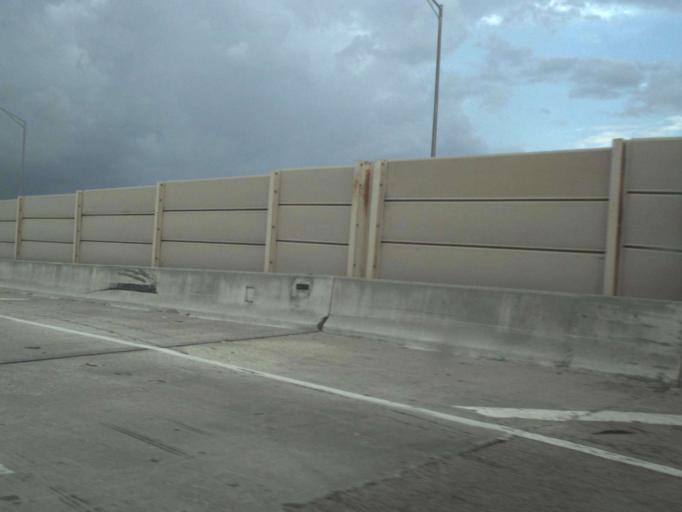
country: US
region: Florida
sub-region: Palm Beach County
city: West Palm Beach
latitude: 26.6934
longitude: -80.0676
